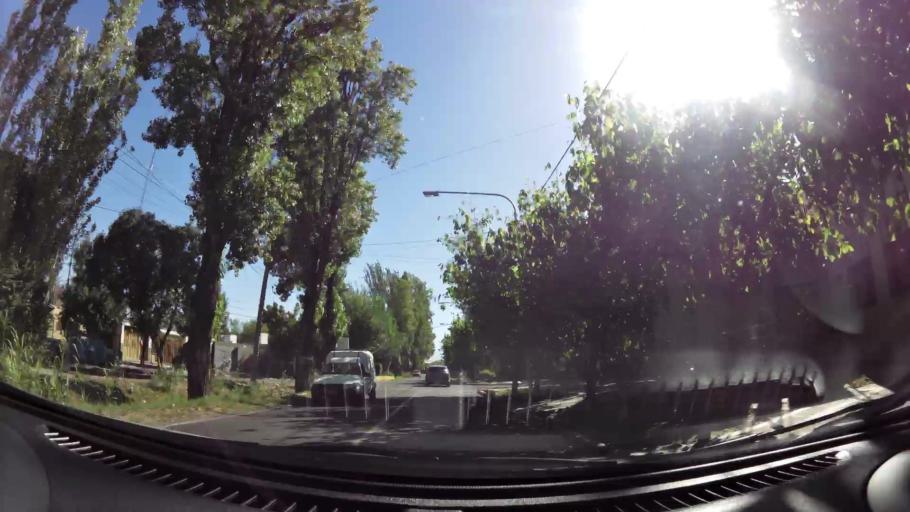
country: AR
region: Mendoza
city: Villa Nueva
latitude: -32.9126
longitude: -68.7953
